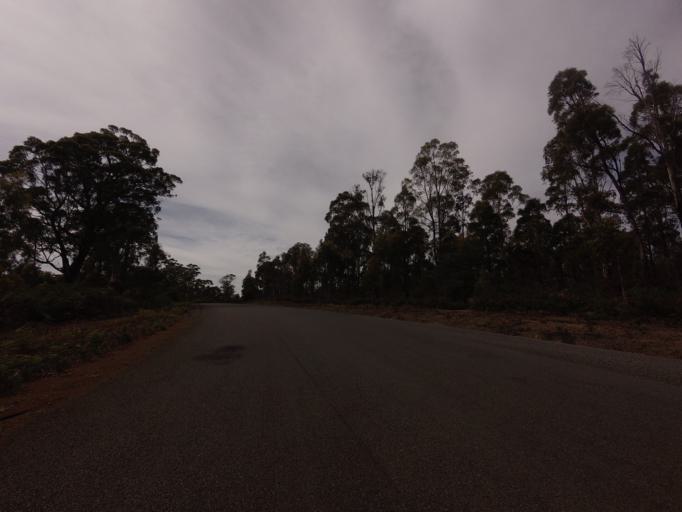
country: AU
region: Tasmania
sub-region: Sorell
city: Sorell
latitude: -42.5146
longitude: 147.6435
